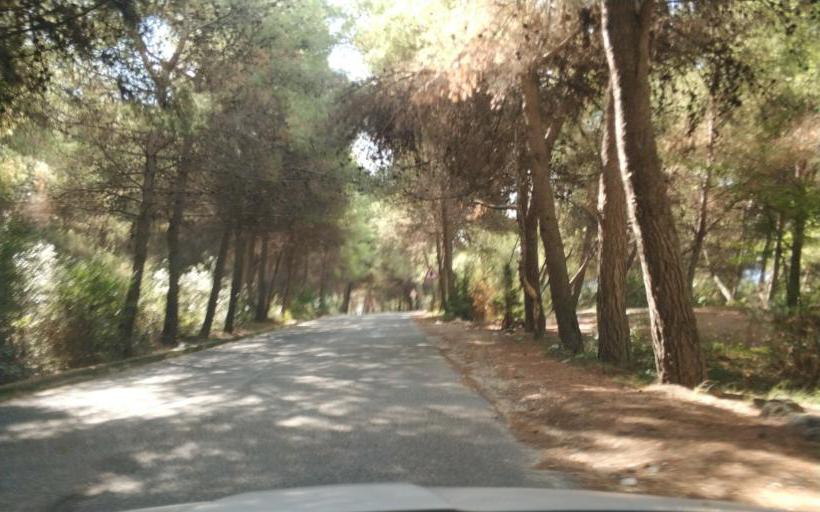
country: AL
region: Durres
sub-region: Rrethi i Krujes
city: Kruje
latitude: 41.4911
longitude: 19.7670
